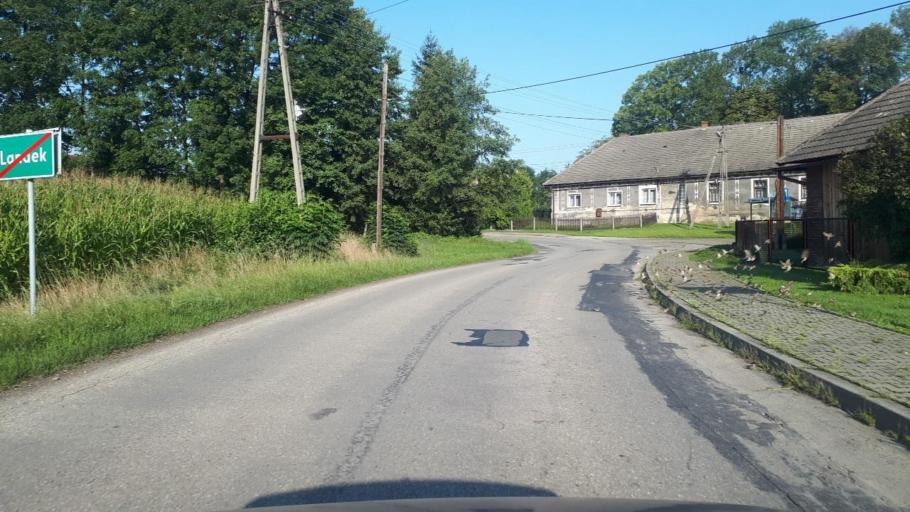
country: PL
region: Silesian Voivodeship
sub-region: Powiat cieszynski
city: Chybie
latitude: 49.8751
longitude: 18.8633
